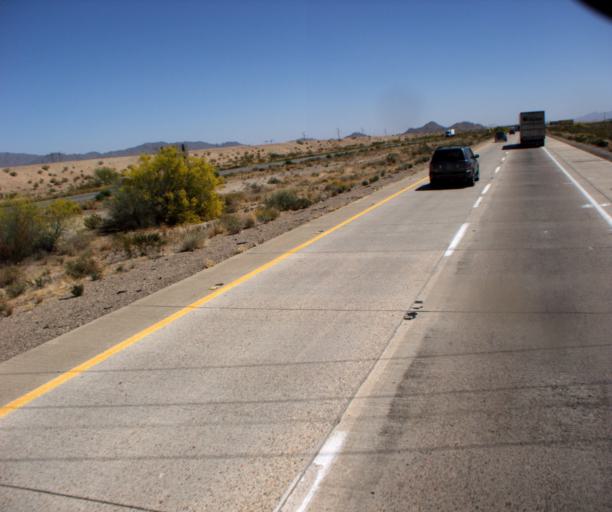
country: US
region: Arizona
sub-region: Maricopa County
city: Buckeye
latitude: 33.4430
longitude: -112.6950
